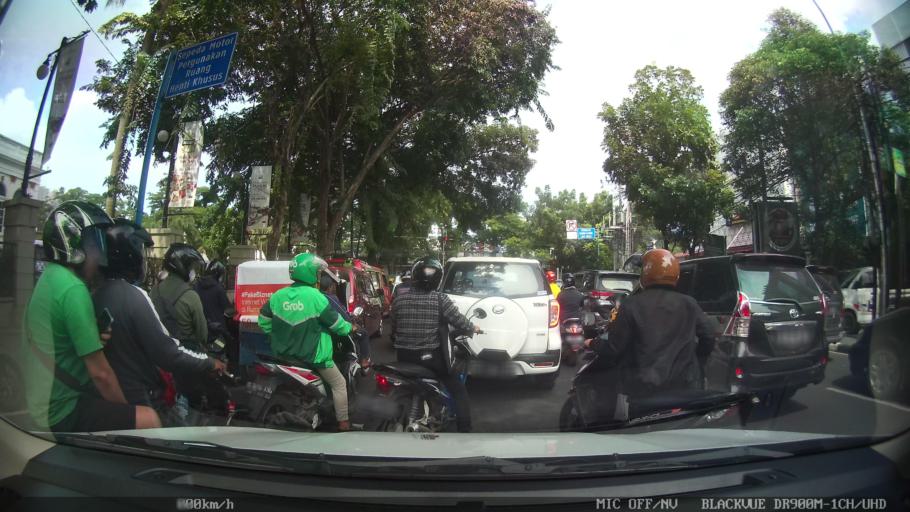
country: ID
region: North Sumatra
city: Medan
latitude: 3.5901
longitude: 98.6772
